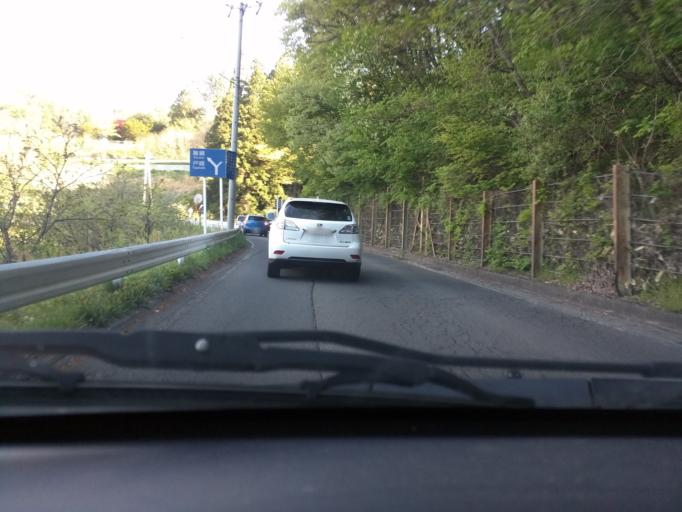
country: JP
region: Nagano
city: Nagano-shi
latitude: 36.6776
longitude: 138.1729
